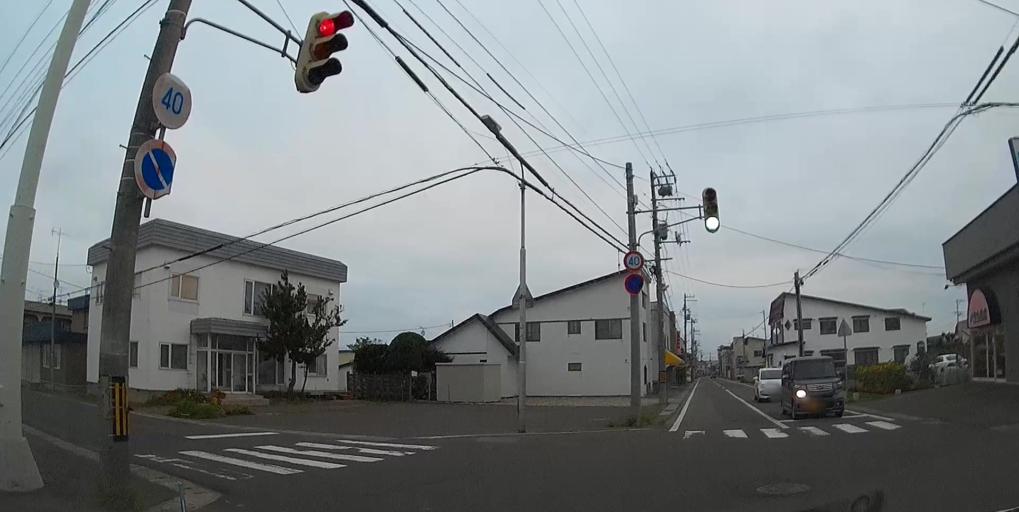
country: JP
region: Hokkaido
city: Nanae
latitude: 42.2553
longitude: 140.2658
